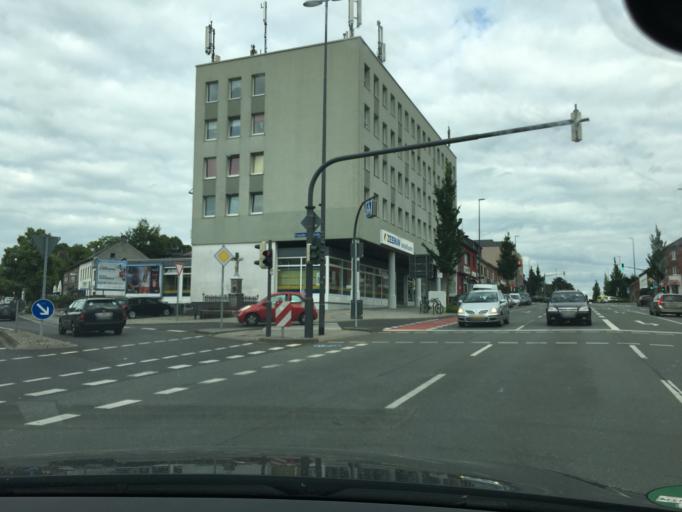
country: DE
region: North Rhine-Westphalia
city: Stolberg
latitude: 50.7493
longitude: 6.1647
